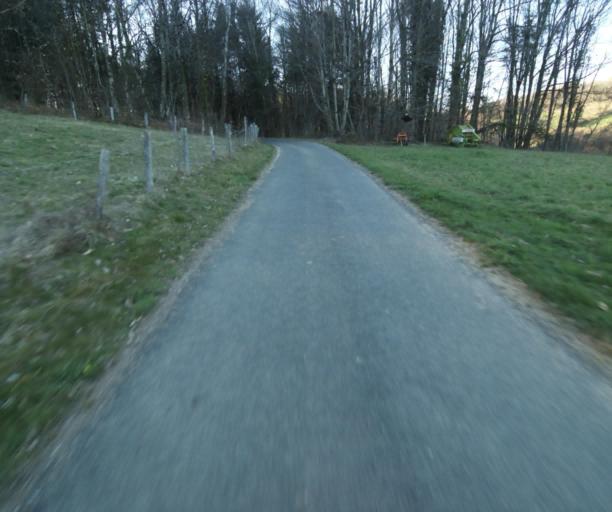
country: FR
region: Limousin
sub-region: Departement de la Correze
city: Saint-Clement
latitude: 45.3575
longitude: 1.6914
